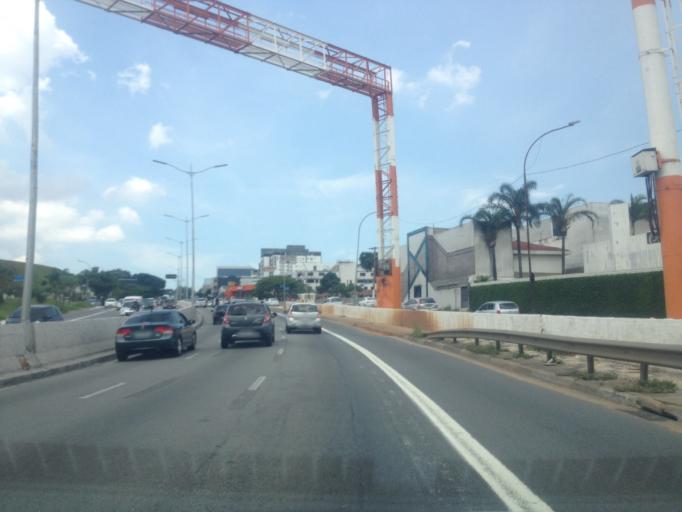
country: BR
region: Sao Paulo
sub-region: Sao Paulo
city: Sao Paulo
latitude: -23.6182
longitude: -46.6621
